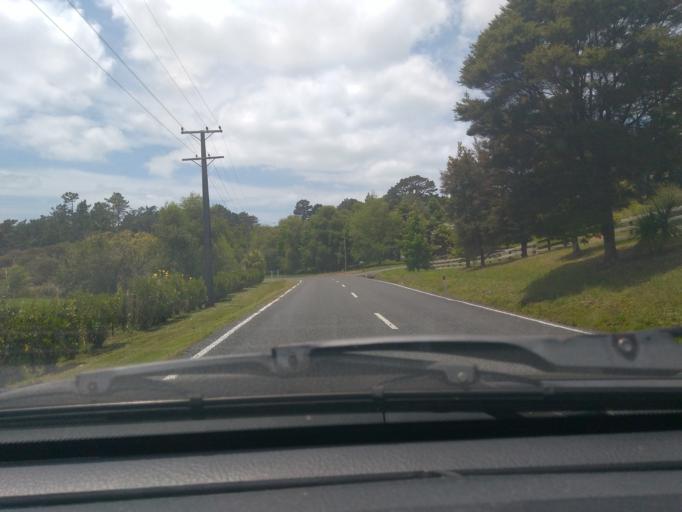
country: NZ
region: Auckland
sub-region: Auckland
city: Rothesay Bay
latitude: -36.6778
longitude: 174.7018
